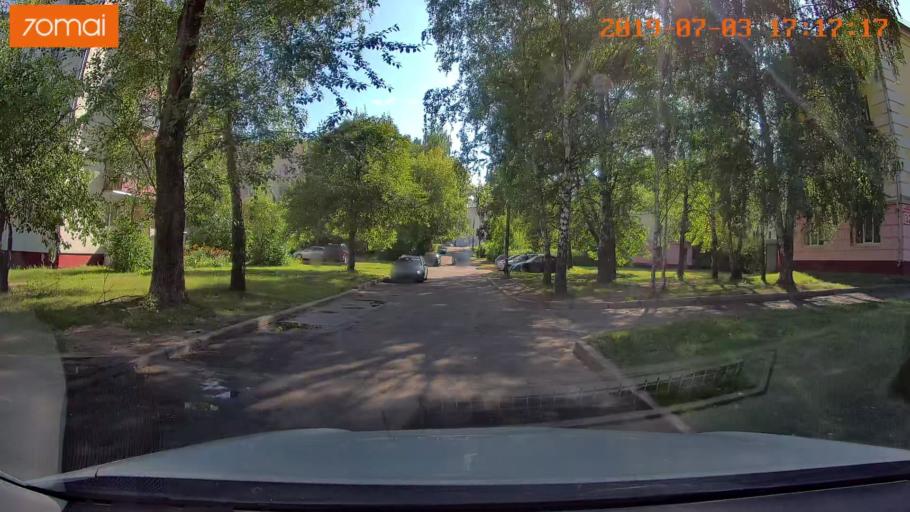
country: BY
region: Minsk
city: Vyaliki Trastsyanets
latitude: 53.9095
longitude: 27.6731
